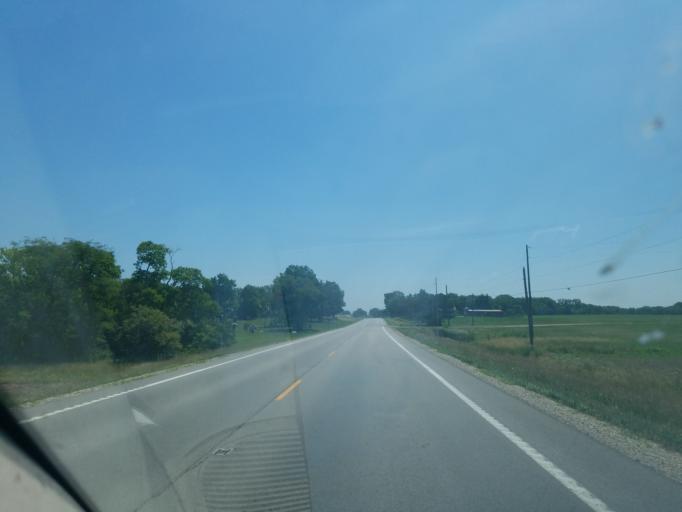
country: US
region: Ohio
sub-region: Mercer County
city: Rockford
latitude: 40.7285
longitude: -84.7434
